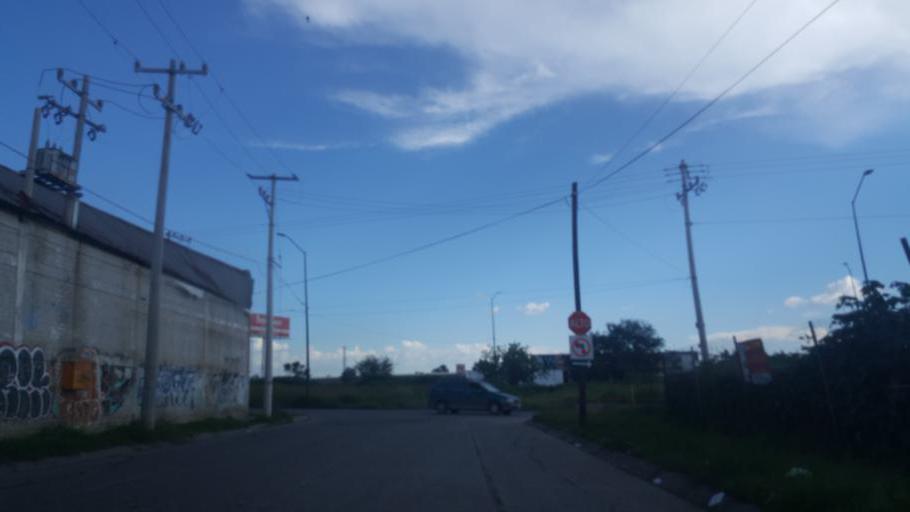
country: MX
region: Guanajuato
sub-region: Leon
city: San Jose de Duran (Los Troncoso)
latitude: 21.0968
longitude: -101.7015
